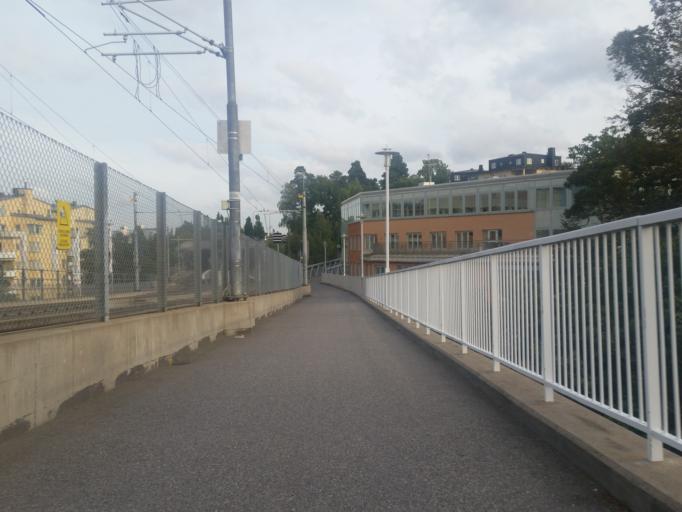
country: SE
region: Stockholm
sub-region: Solna Kommun
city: Solna
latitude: 59.3252
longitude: 17.9911
